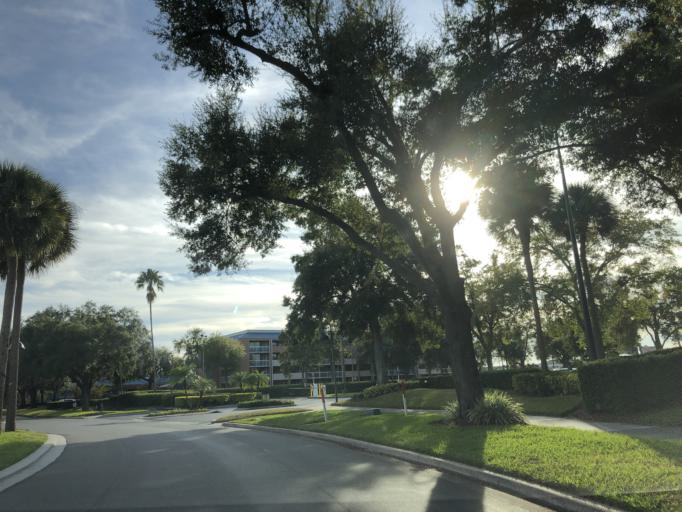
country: US
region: Florida
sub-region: Orange County
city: Doctor Phillips
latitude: 28.4469
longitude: -81.4724
